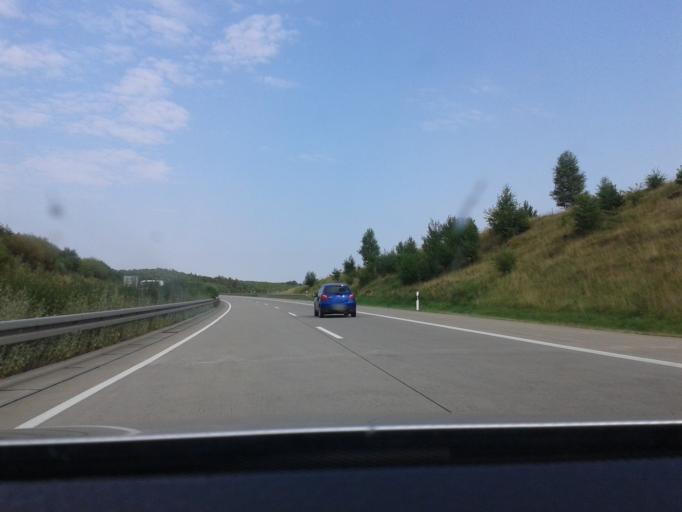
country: DE
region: Thuringia
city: Schachtebich
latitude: 51.3928
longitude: 10.0529
